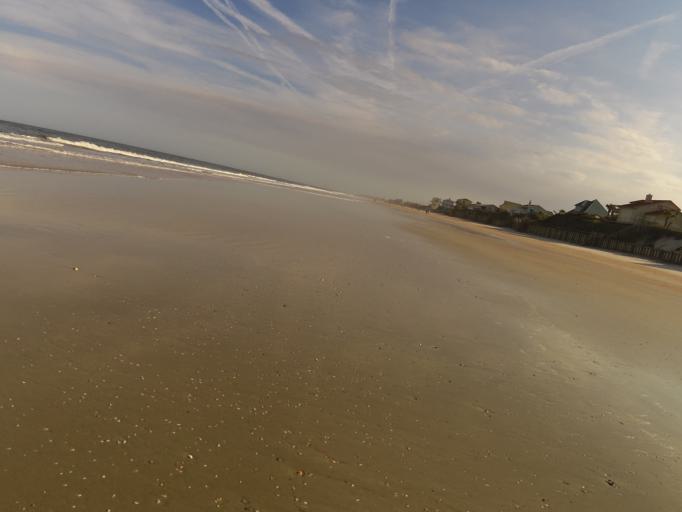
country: US
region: Florida
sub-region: Saint Johns County
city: Villano Beach
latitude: 29.9457
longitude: -81.2990
